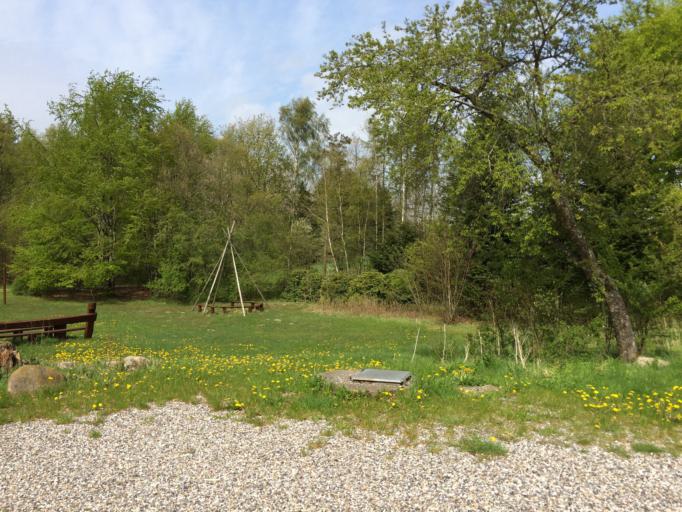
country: DK
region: Central Jutland
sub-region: Holstebro Kommune
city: Ulfborg
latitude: 56.2338
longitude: 8.4178
